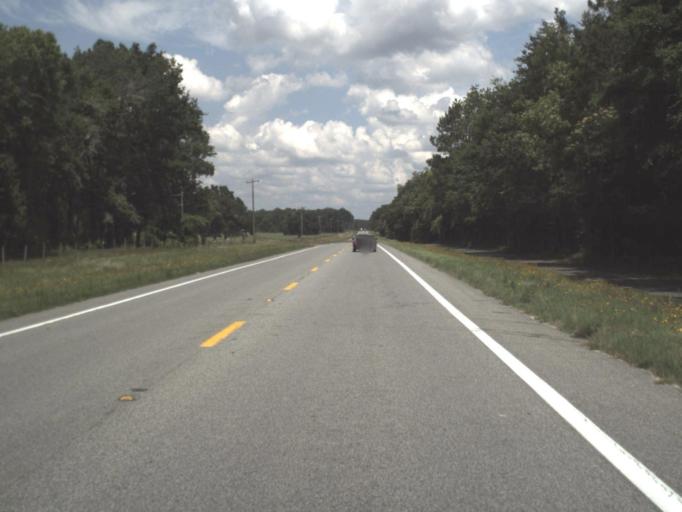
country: US
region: Florida
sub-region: Alachua County
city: High Springs
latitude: 29.9507
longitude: -82.7697
